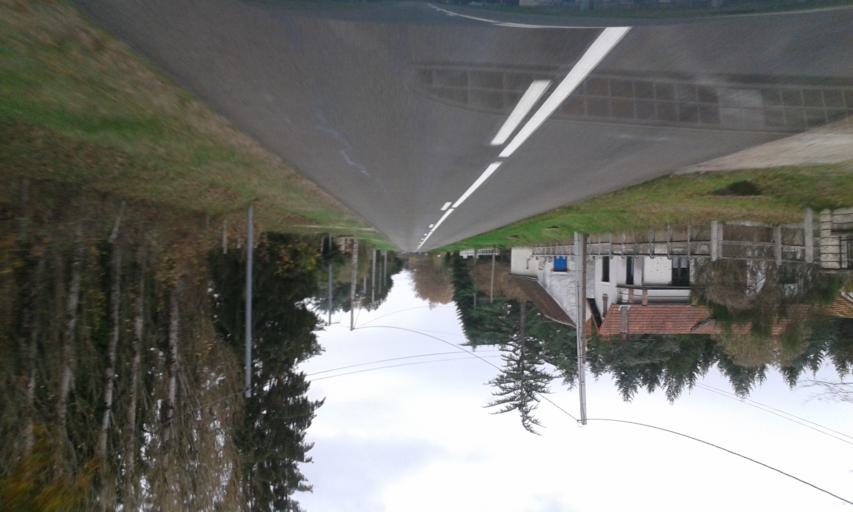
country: FR
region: Centre
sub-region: Departement du Loiret
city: Vitry-aux-Loges
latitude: 47.9327
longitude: 2.2365
